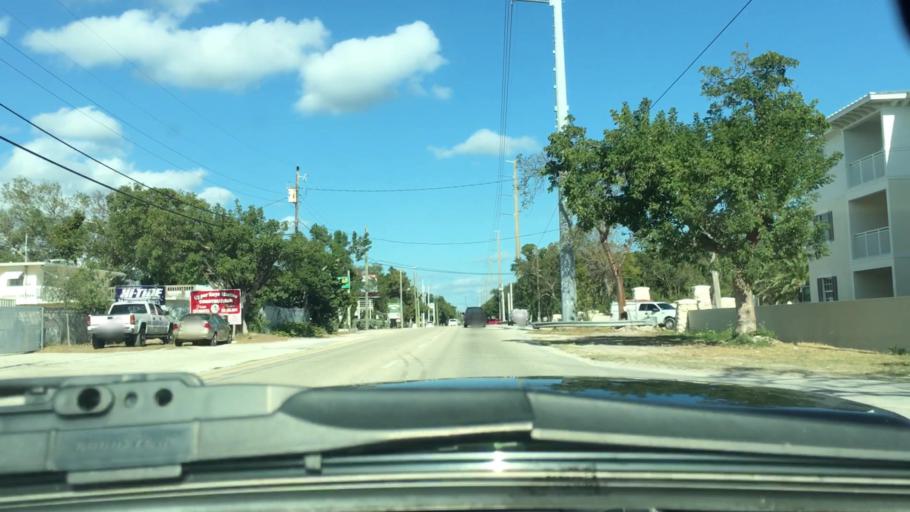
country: US
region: Florida
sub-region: Monroe County
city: Key Largo
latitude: 25.0757
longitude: -80.4608
